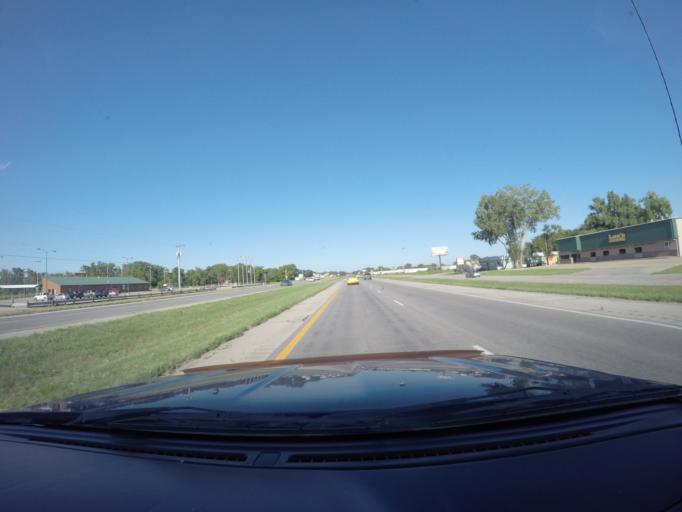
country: US
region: Kansas
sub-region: Shawnee County
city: Topeka
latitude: 39.0910
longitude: -95.6552
